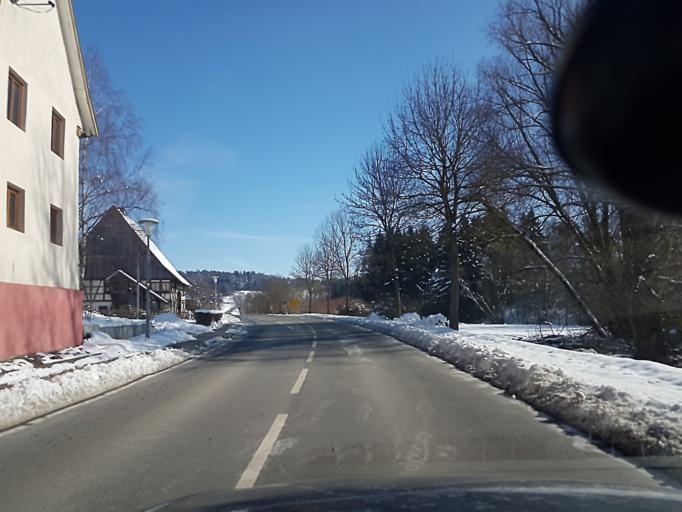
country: DE
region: Baden-Wuerttemberg
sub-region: Freiburg Region
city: Niedereschach
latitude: 48.1667
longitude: 8.5348
